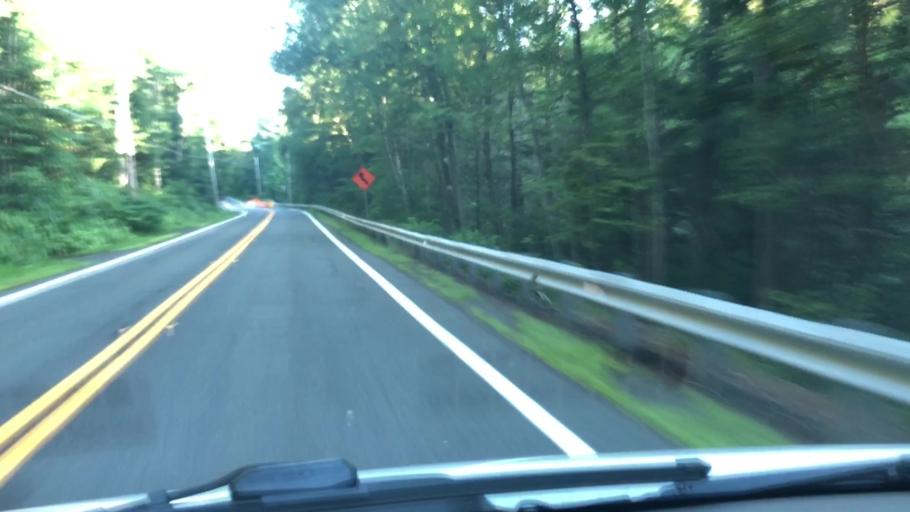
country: US
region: Massachusetts
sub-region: Hampshire County
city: Chesterfield
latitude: 42.3465
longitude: -72.8960
